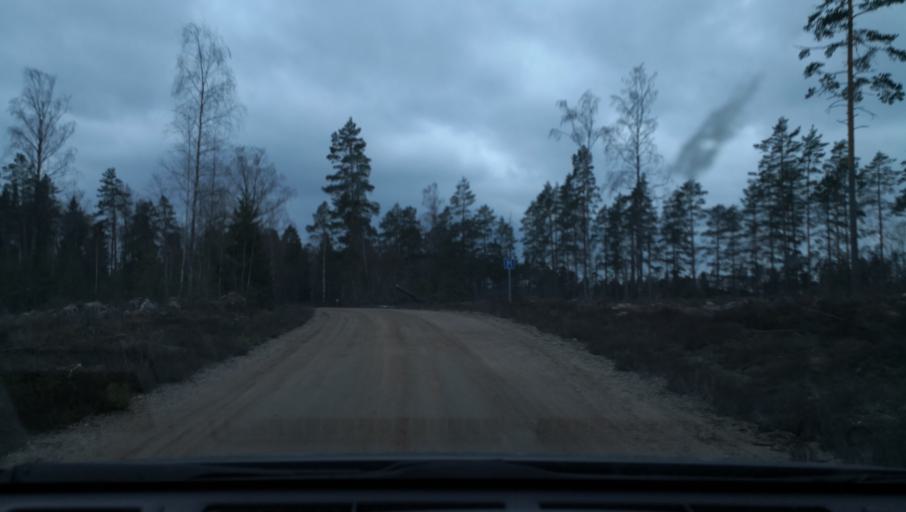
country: SE
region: OErebro
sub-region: Lindesbergs Kommun
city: Fellingsbro
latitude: 59.5988
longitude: 15.5801
